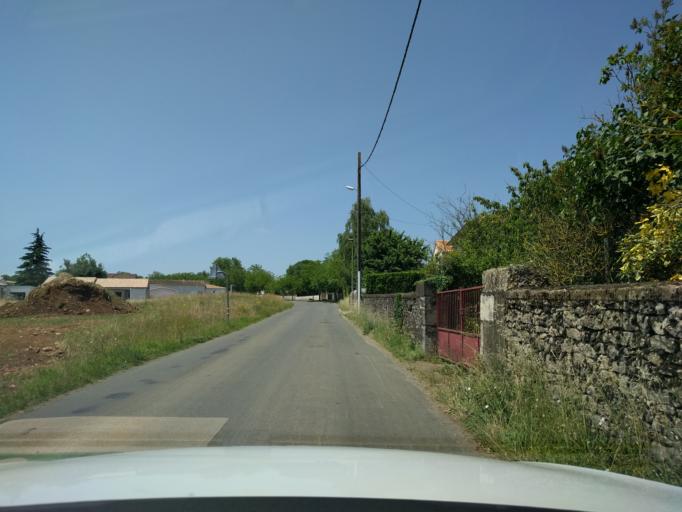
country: FR
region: Poitou-Charentes
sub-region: Departement des Deux-Sevres
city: Niort
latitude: 46.3519
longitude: -0.4616
